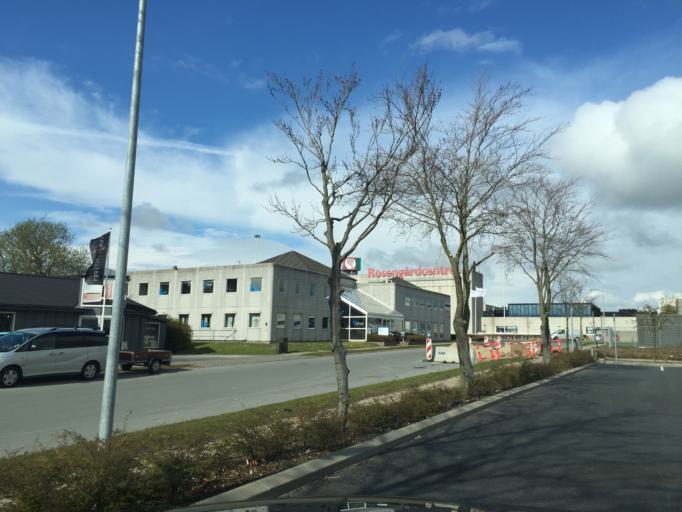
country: DK
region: South Denmark
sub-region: Odense Kommune
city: Neder Holluf
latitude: 55.3826
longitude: 10.4235
